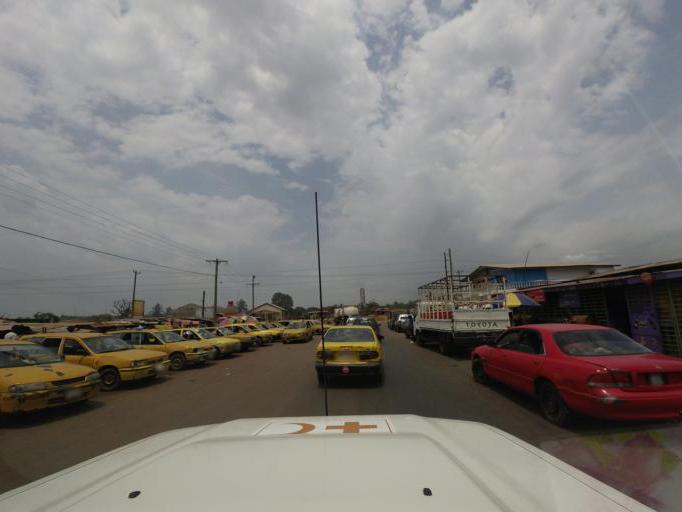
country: LR
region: Montserrado
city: Monrovia
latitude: 6.2981
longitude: -10.7023
